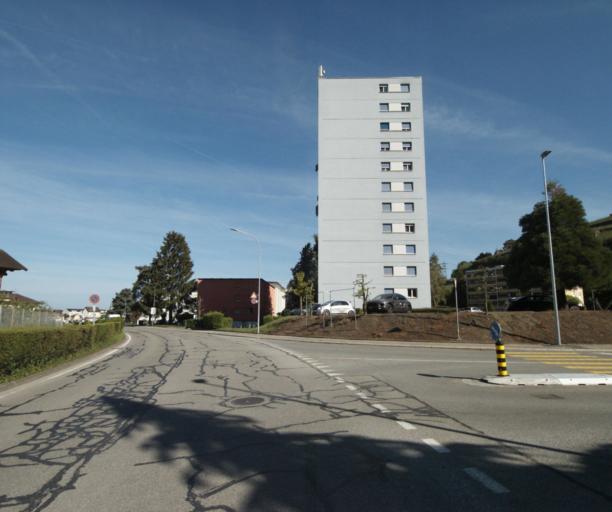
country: CH
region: Vaud
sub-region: Aigle District
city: Villeneuve
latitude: 46.3952
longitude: 6.9341
